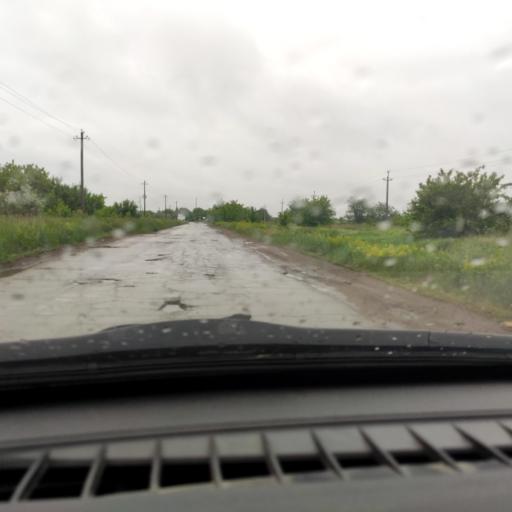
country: RU
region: Samara
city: Tol'yatti
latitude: 53.5667
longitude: 49.3574
